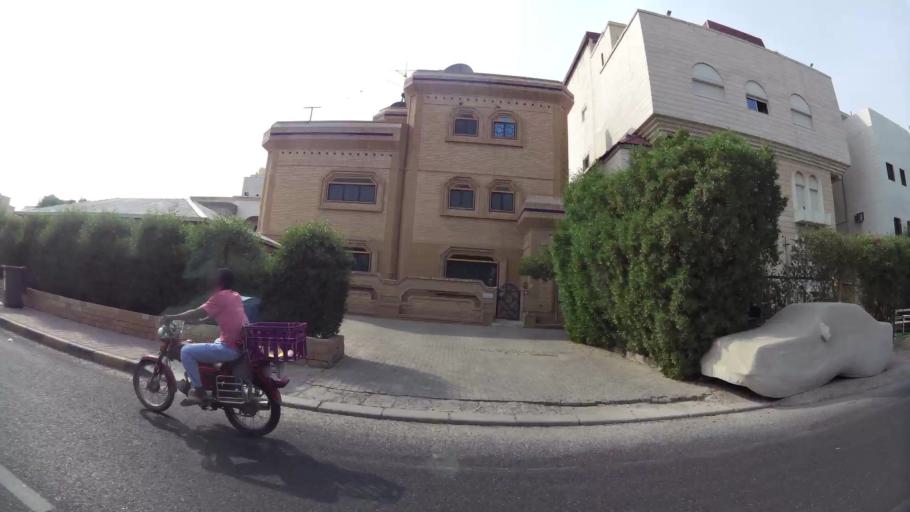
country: KW
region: Al Asimah
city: Ar Rabiyah
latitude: 29.2818
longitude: 47.9380
